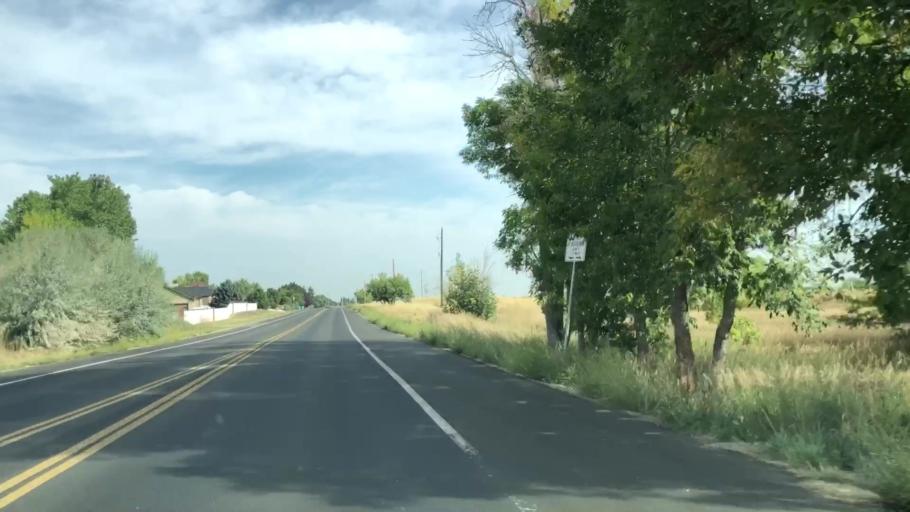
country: US
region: Colorado
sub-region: Larimer County
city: Loveland
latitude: 40.4332
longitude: -105.0454
